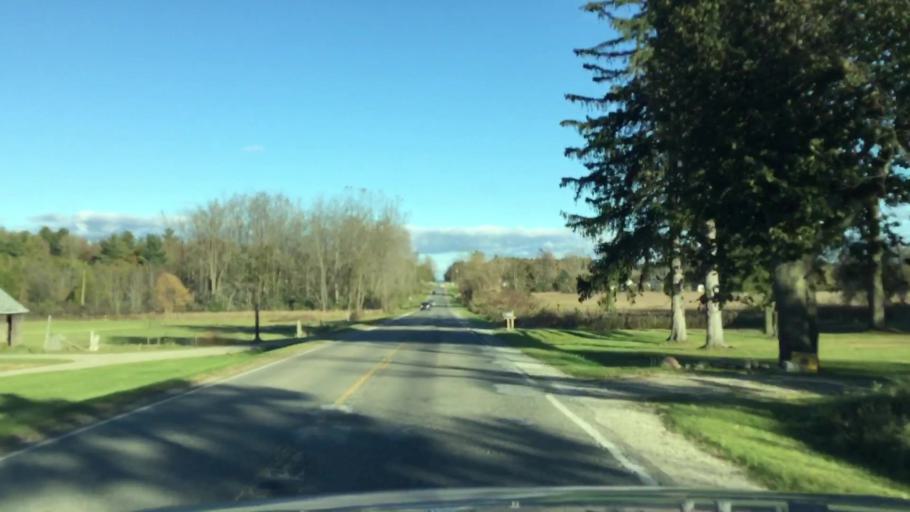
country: US
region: Michigan
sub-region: Lapeer County
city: Lapeer
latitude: 43.0618
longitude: -83.1979
